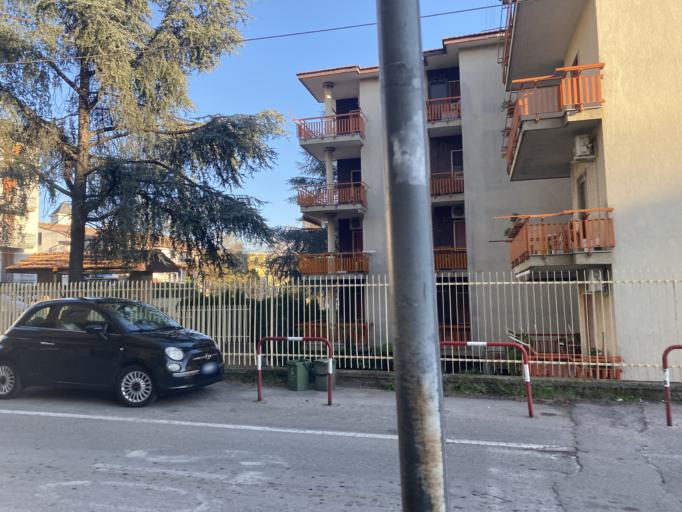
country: IT
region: Campania
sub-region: Provincia di Salerno
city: Agropoli
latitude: 40.3497
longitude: 14.9893
